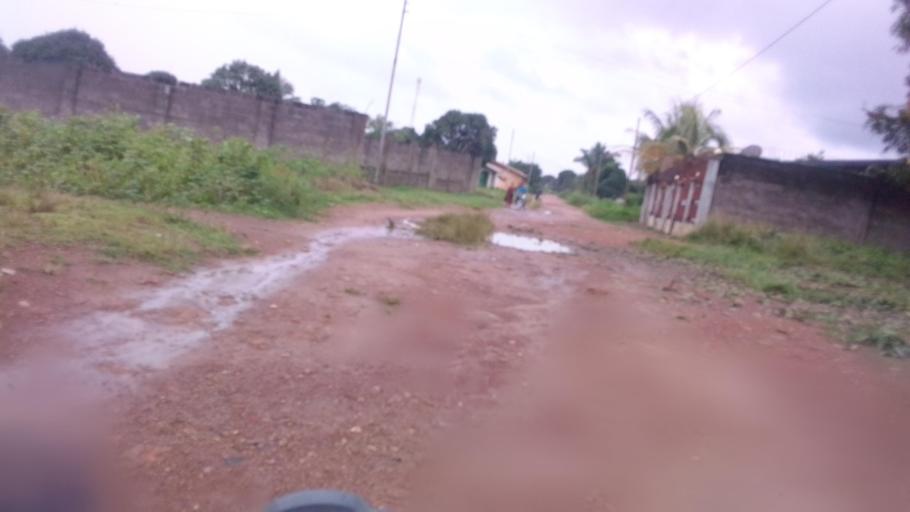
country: SL
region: Eastern Province
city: Kenema
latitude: 7.8874
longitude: -11.1720
